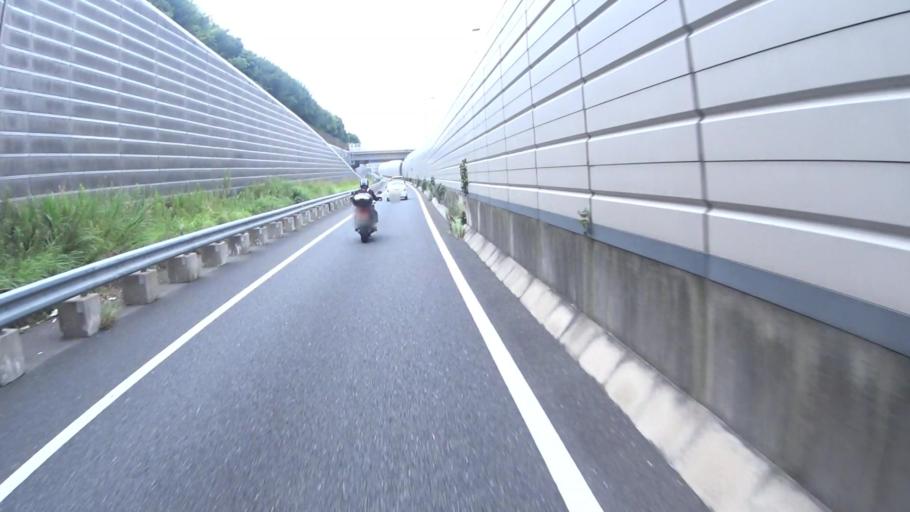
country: JP
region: Kyoto
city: Yawata
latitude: 34.8326
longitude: 135.7239
